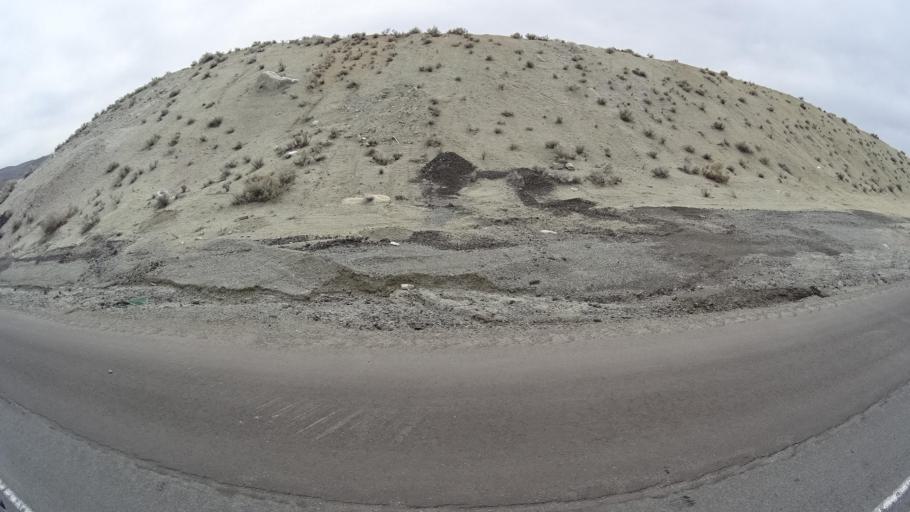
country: US
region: Nevada
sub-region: Washoe County
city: Sun Valley
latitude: 39.6114
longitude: -119.7363
